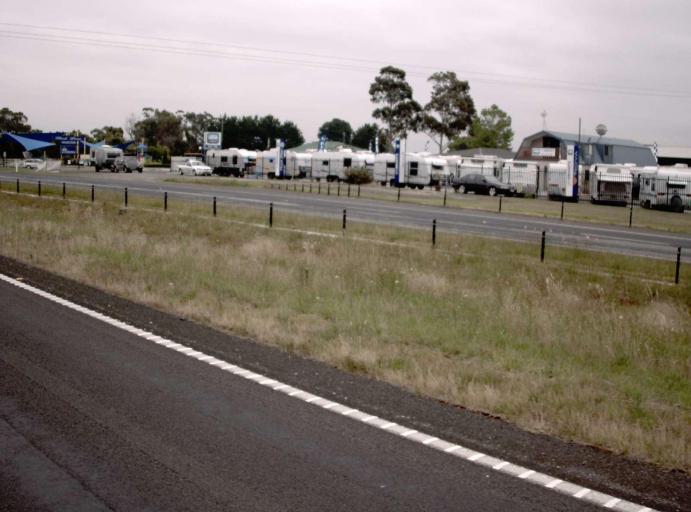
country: AU
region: Victoria
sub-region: Latrobe
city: Traralgon
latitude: -38.2157
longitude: 146.4796
